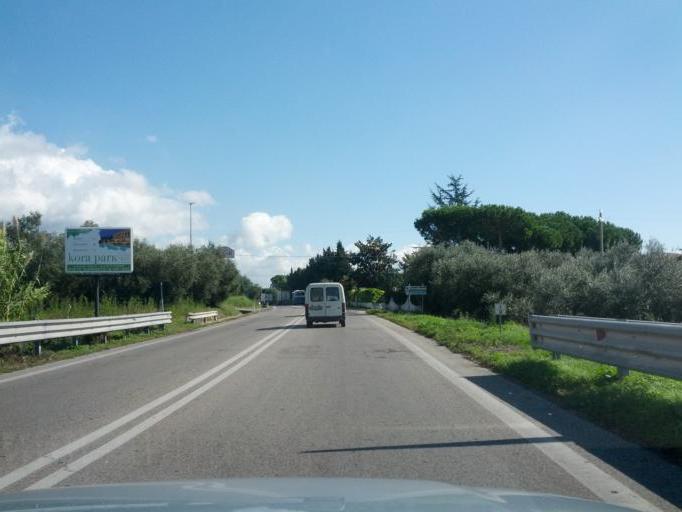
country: IT
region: Latium
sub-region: Provincia di Latina
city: Formia
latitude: 41.2656
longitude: 13.6522
